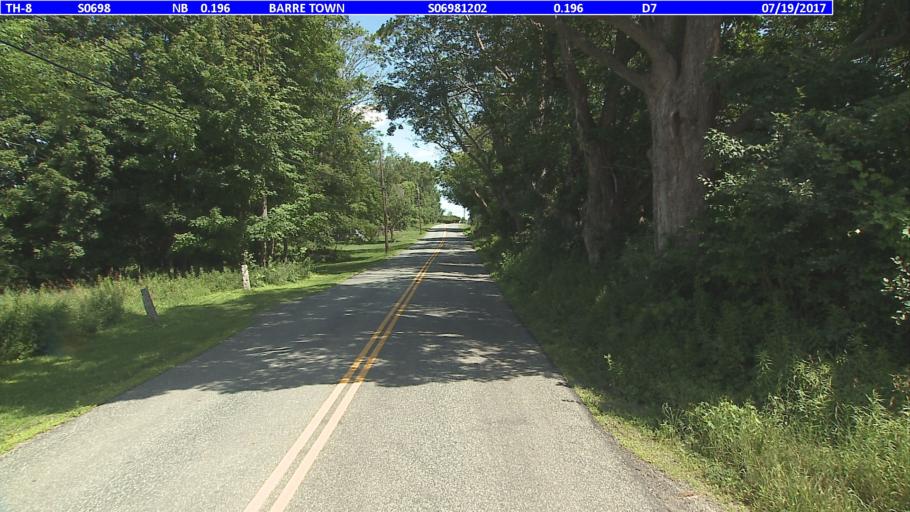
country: US
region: Vermont
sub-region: Washington County
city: Barre
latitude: 44.2219
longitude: -72.4612
